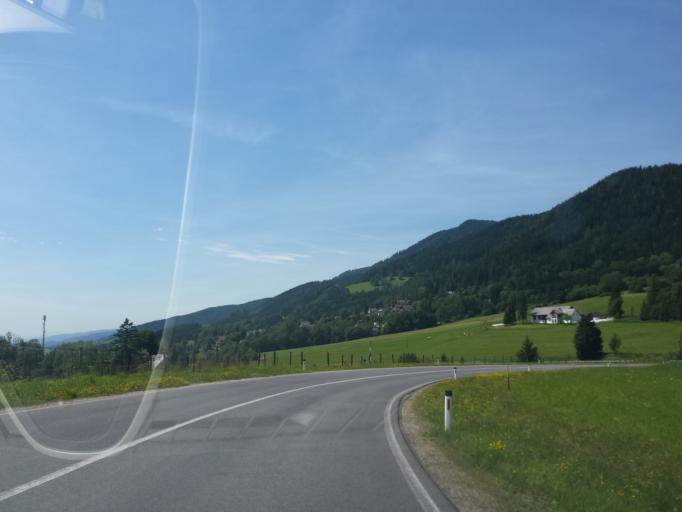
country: AT
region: Lower Austria
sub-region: Politischer Bezirk Neunkirchen
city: Semmering
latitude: 47.6243
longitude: 15.7953
